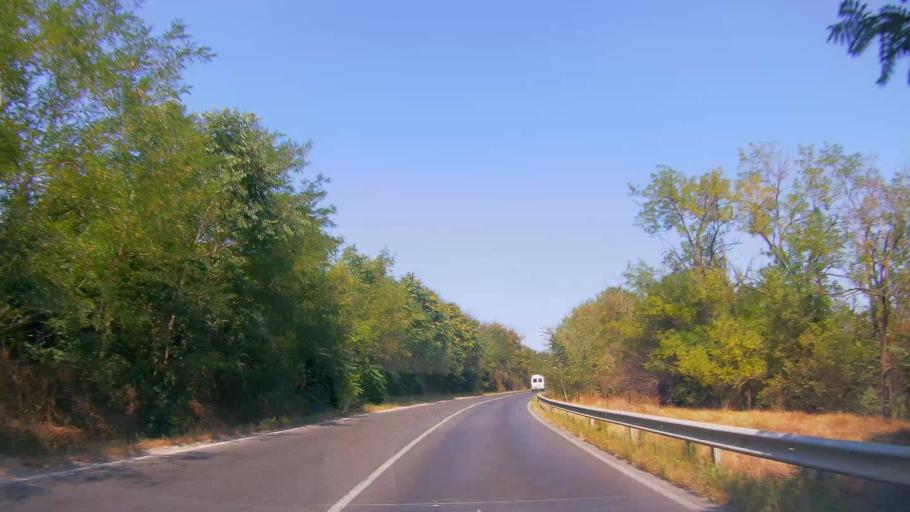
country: BG
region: Razgrad
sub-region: Obshtina Tsar Kaloyan
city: Tsar Kaloyan
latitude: 43.6220
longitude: 26.2116
